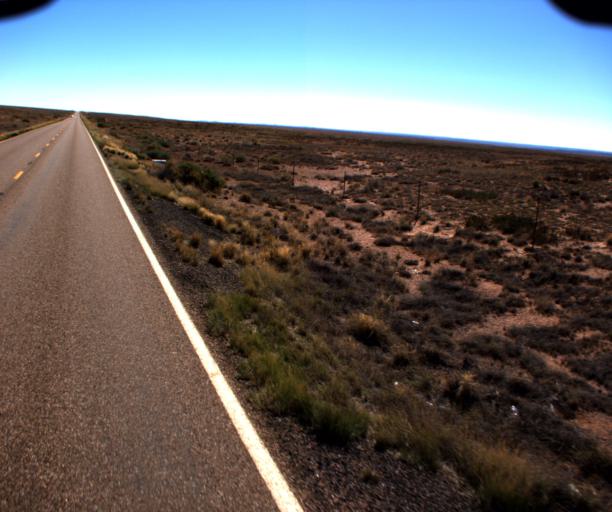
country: US
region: Arizona
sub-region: Navajo County
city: Holbrook
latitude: 35.0251
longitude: -110.0905
